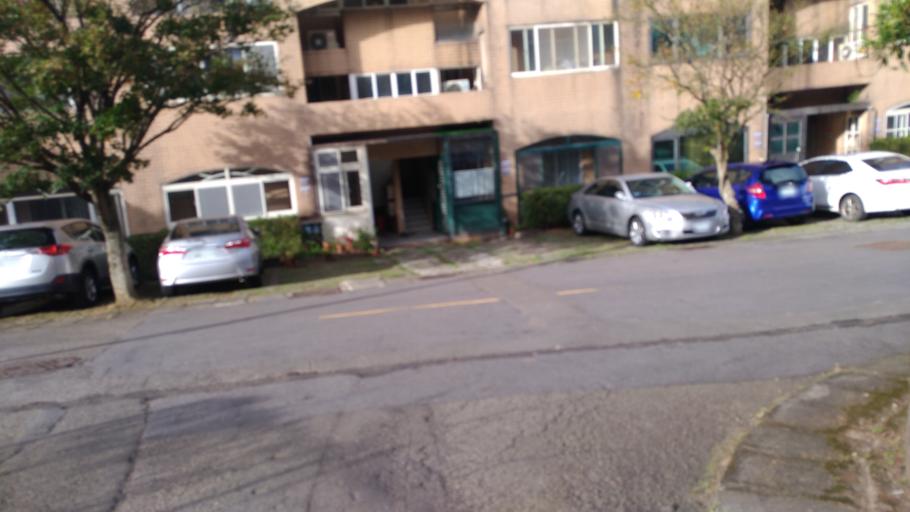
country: TW
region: Taiwan
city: Daxi
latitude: 24.8861
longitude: 121.1717
